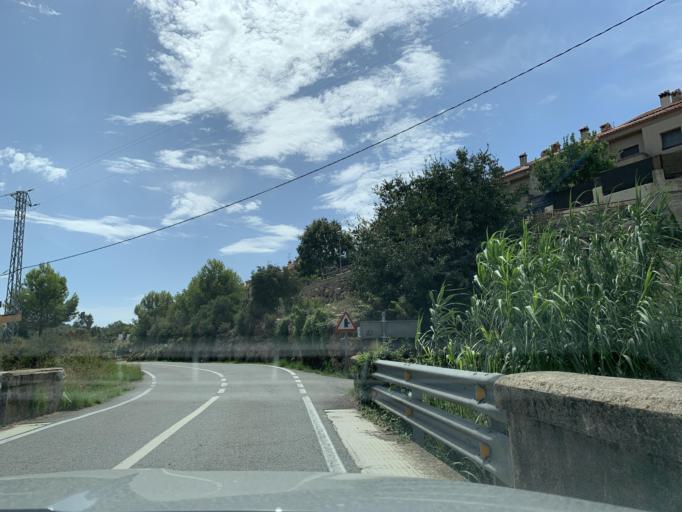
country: ES
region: Catalonia
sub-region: Provincia de Tarragona
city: Altafulla
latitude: 41.1583
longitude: 1.3630
